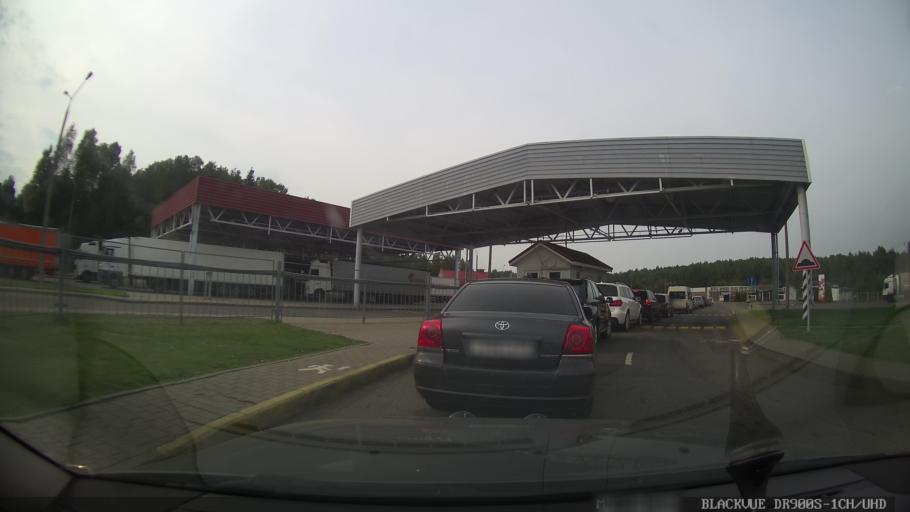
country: BY
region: Grodnenskaya
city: Astravyets
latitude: 54.5429
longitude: 25.7014
